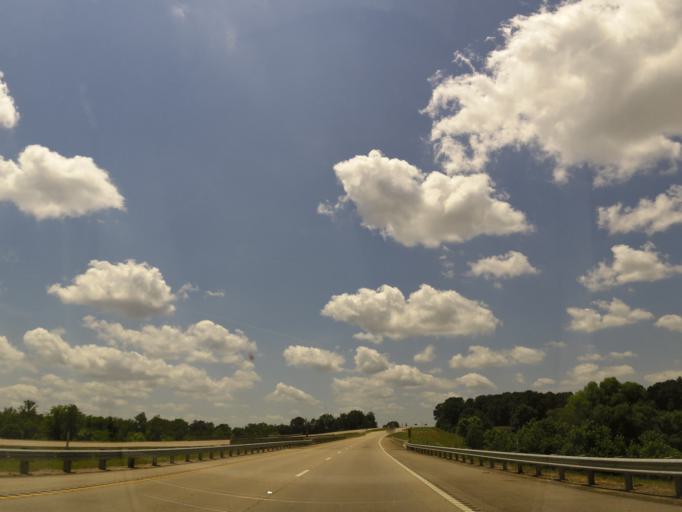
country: US
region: Mississippi
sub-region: Pontotoc County
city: Pontotoc
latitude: 34.2895
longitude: -88.9862
